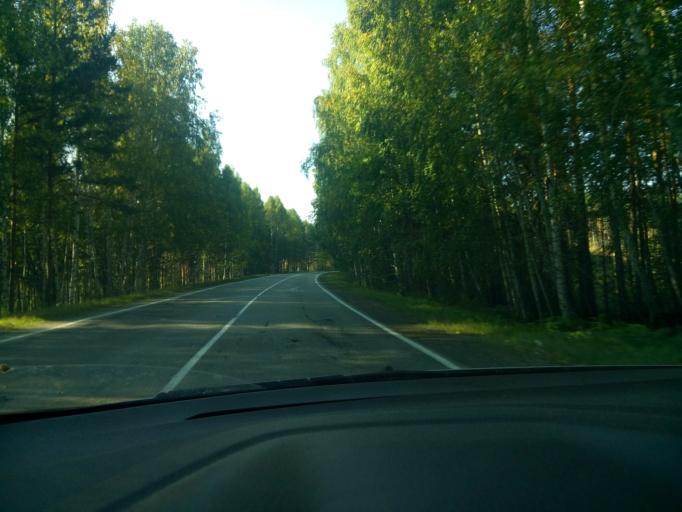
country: RU
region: Chelyabinsk
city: Ozersk
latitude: 55.8460
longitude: 60.6561
